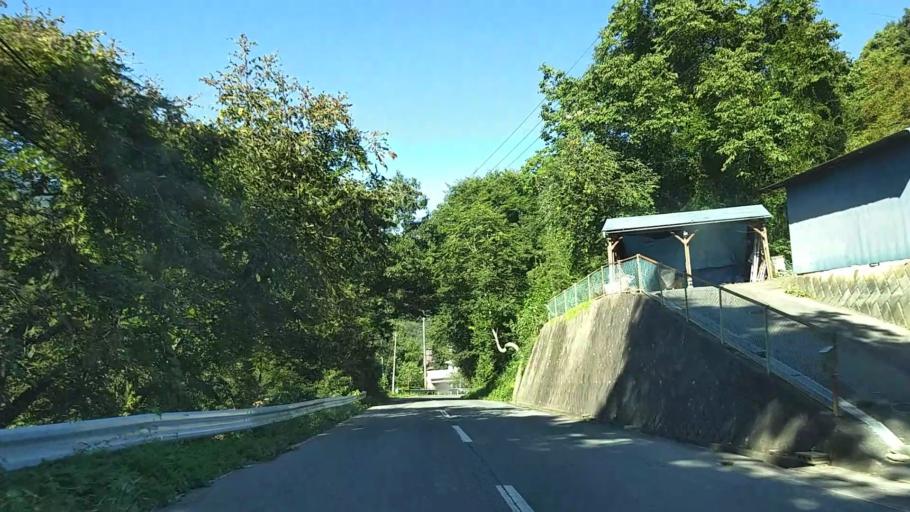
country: JP
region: Nagano
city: Nagano-shi
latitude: 36.6144
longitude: 138.0911
